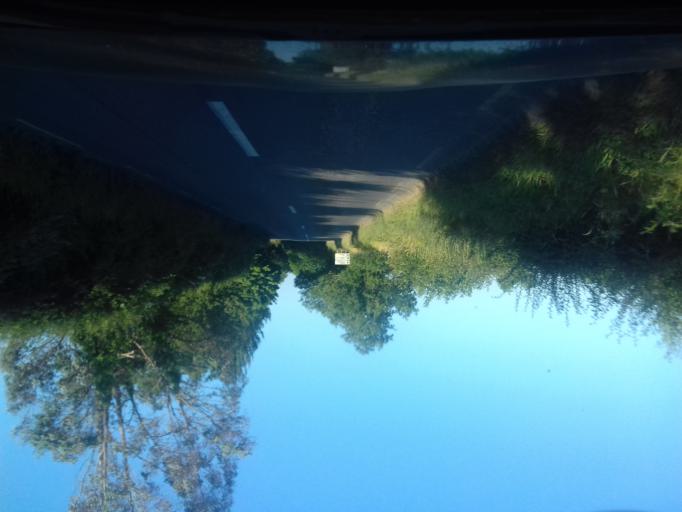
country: IE
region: Leinster
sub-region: Dublin City
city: Finglas
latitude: 53.4423
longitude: -6.3002
